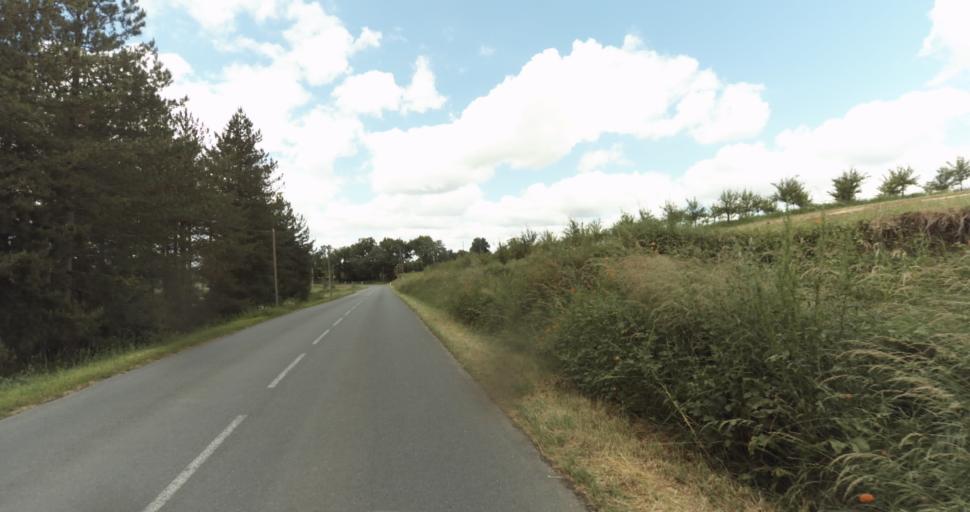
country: FR
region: Aquitaine
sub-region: Departement du Lot-et-Garonne
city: Villereal
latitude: 44.6832
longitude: 0.7585
